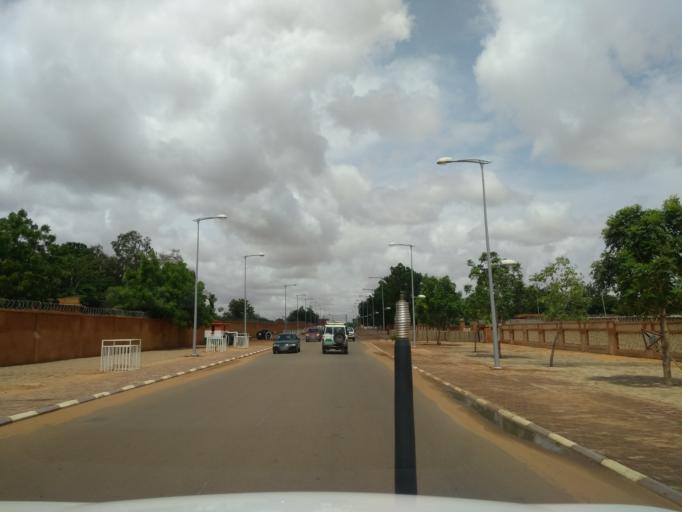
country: NE
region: Niamey
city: Niamey
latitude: 13.5031
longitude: 2.1258
